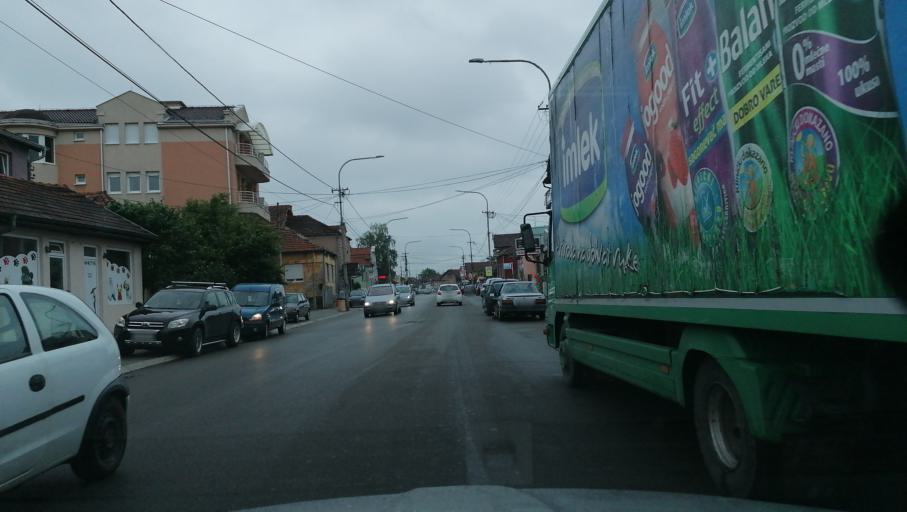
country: RS
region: Central Serbia
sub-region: Rasinski Okrug
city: Krusevac
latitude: 43.5834
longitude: 21.3101
